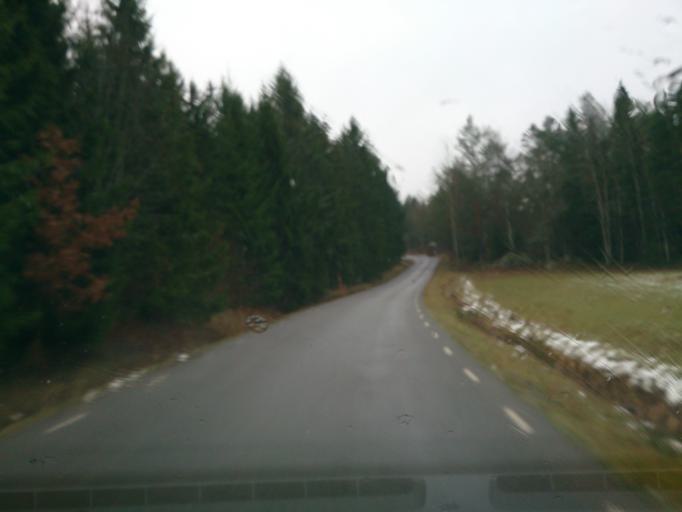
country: SE
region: OEstergoetland
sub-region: Atvidabergs Kommun
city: Atvidaberg
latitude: 58.2488
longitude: 16.1011
